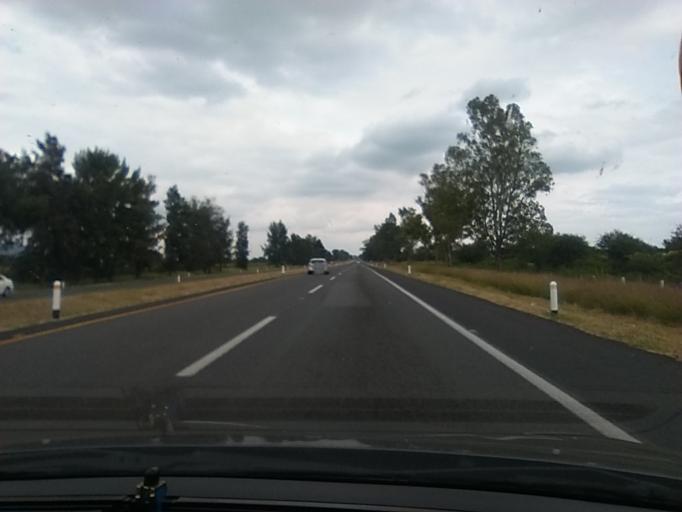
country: MX
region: Jalisco
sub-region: Ocotlan
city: Joconoxtle (La Tuna)
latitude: 20.3778
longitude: -102.6824
